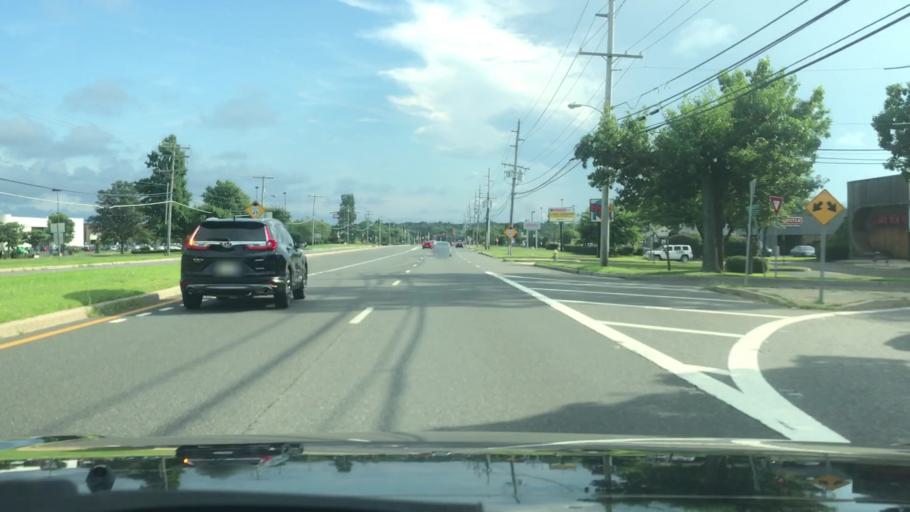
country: US
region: New Jersey
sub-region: Ocean County
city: Toms River
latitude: 39.9850
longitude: -74.1795
